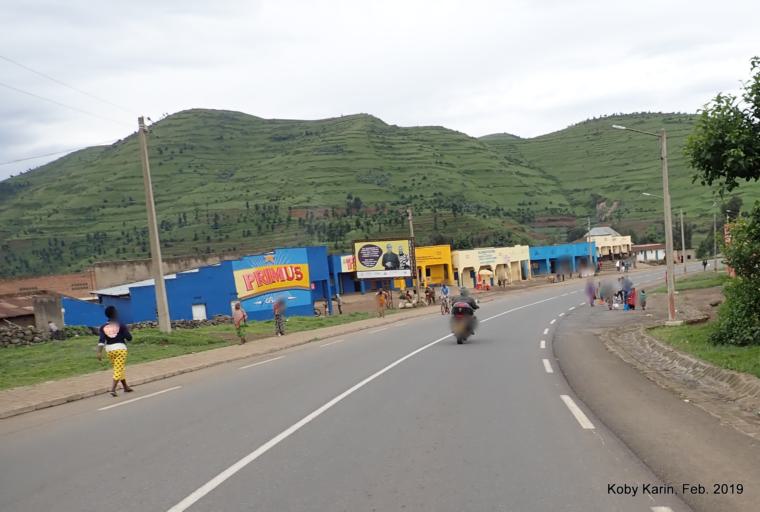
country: RW
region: Western Province
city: Gisenyi
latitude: -1.6172
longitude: 29.4386
